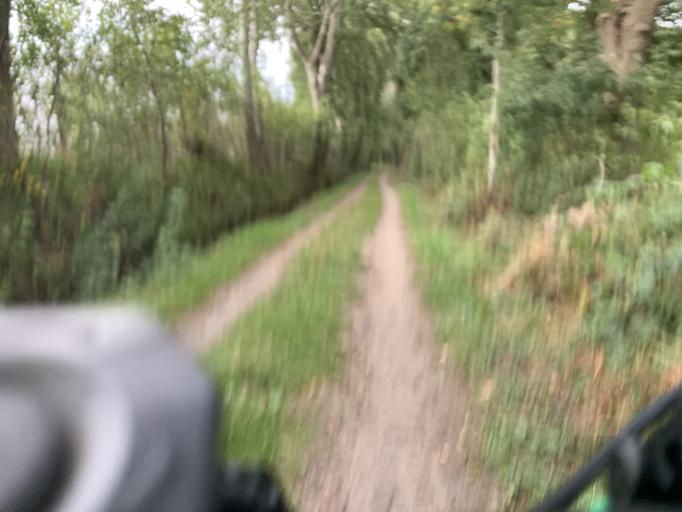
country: DE
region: Lower Saxony
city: Westerstede
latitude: 53.2436
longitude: 7.9094
